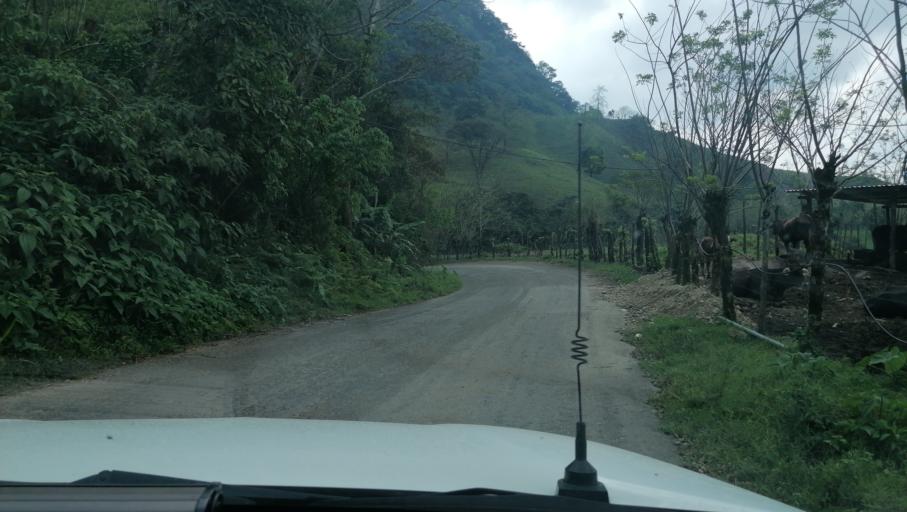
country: MX
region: Chiapas
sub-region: Francisco Leon
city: San Miguel la Sardina
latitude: 17.2459
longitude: -93.2866
